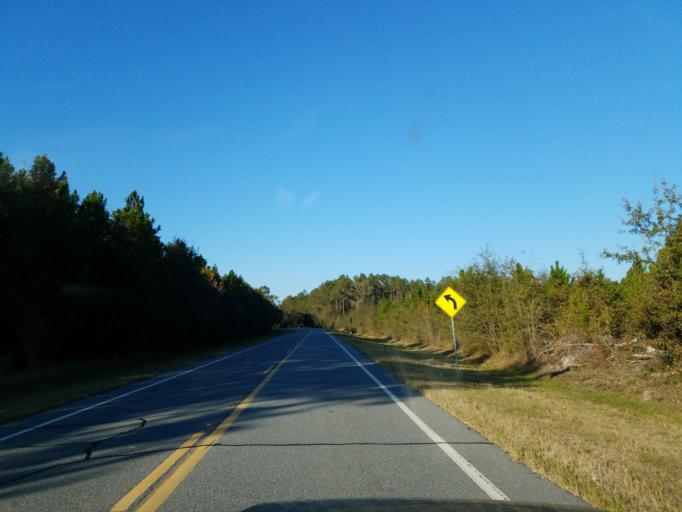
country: US
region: Georgia
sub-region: Echols County
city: Statenville
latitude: 30.8419
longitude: -83.0531
